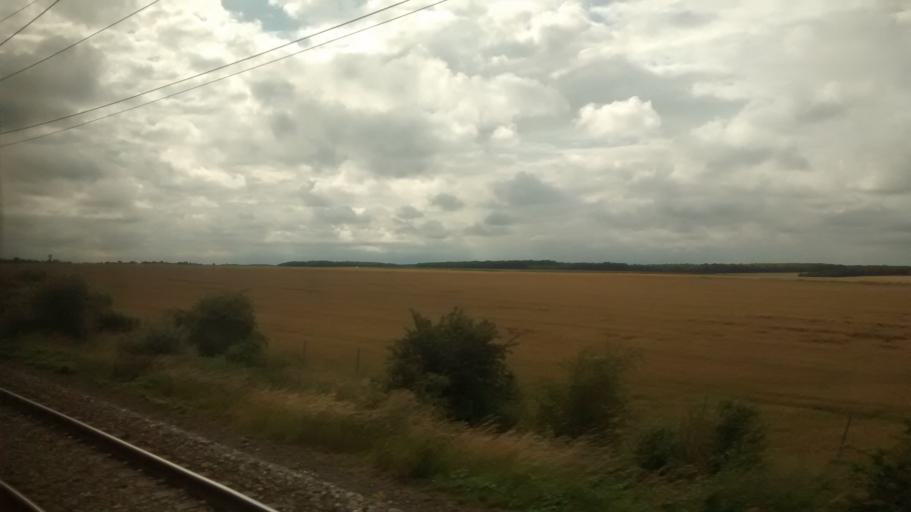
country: FR
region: Centre
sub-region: Departement d'Eure-et-Loir
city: Voves
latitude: 48.2443
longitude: 1.5315
